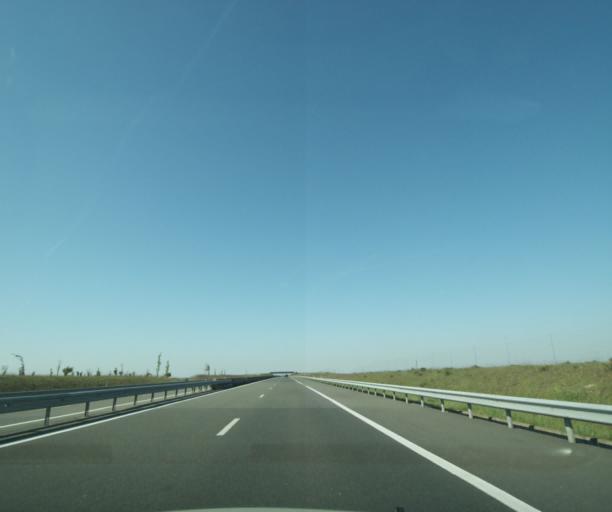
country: FR
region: Centre
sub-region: Departement du Loiret
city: Ascheres-le-Marche
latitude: 48.0832
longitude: 1.9916
